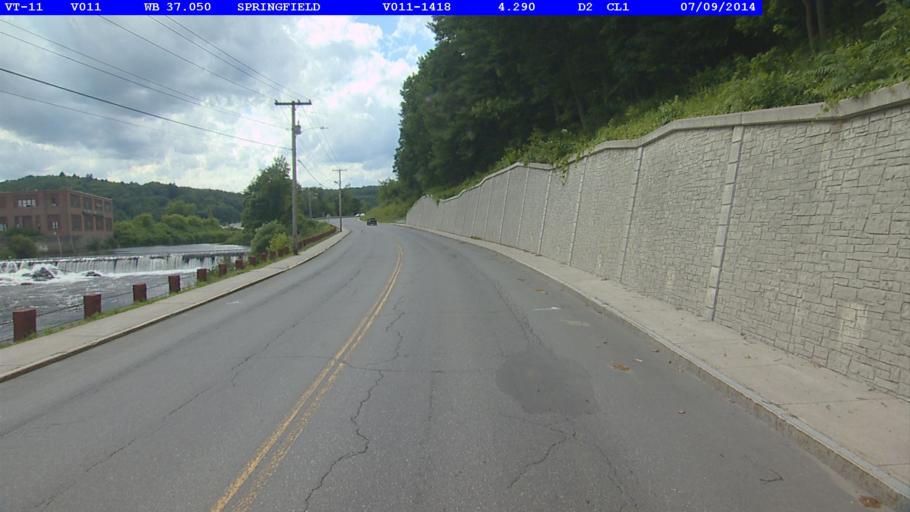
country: US
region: Vermont
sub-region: Windsor County
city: Springfield
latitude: 43.3024
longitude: -72.4859
